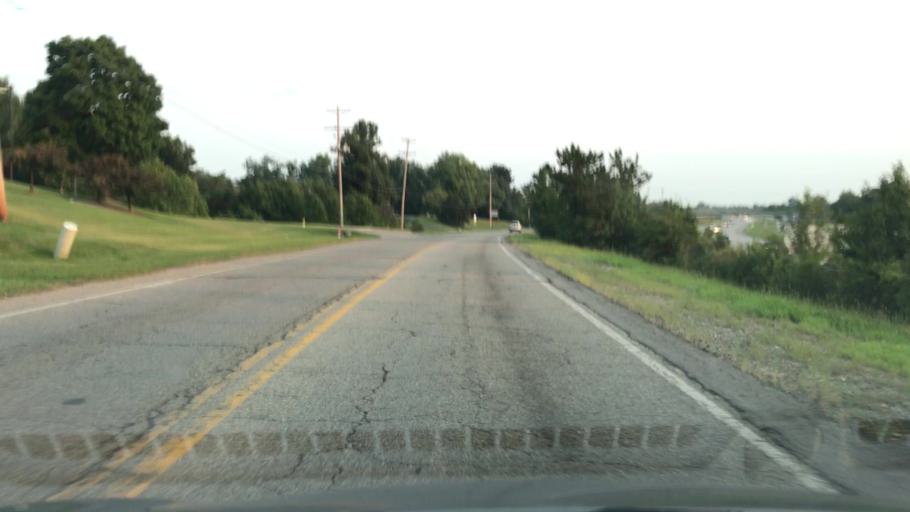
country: US
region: Ohio
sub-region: Franklin County
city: Gahanna
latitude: 39.9969
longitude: -82.8558
